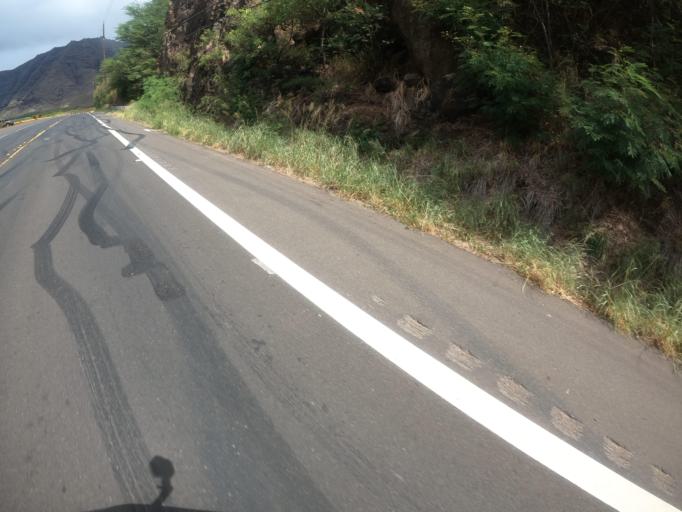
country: US
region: Hawaii
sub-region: Honolulu County
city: Makaha Valley
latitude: 21.5194
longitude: -158.2278
